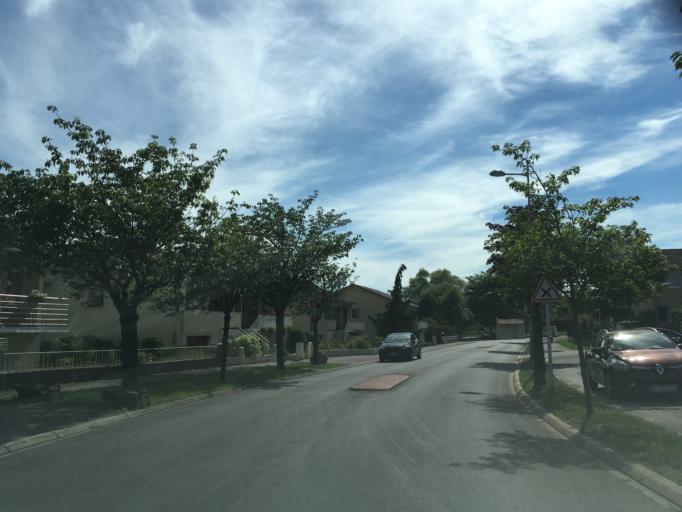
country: FR
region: Lorraine
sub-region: Departement de la Moselle
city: Peltre
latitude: 49.0724
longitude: 6.1947
